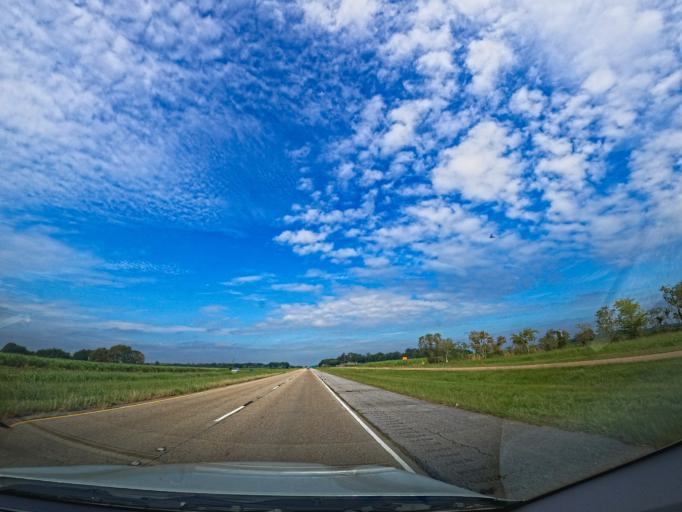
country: US
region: Louisiana
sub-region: Saint Mary Parish
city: Franklin
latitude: 29.7334
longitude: -91.4209
